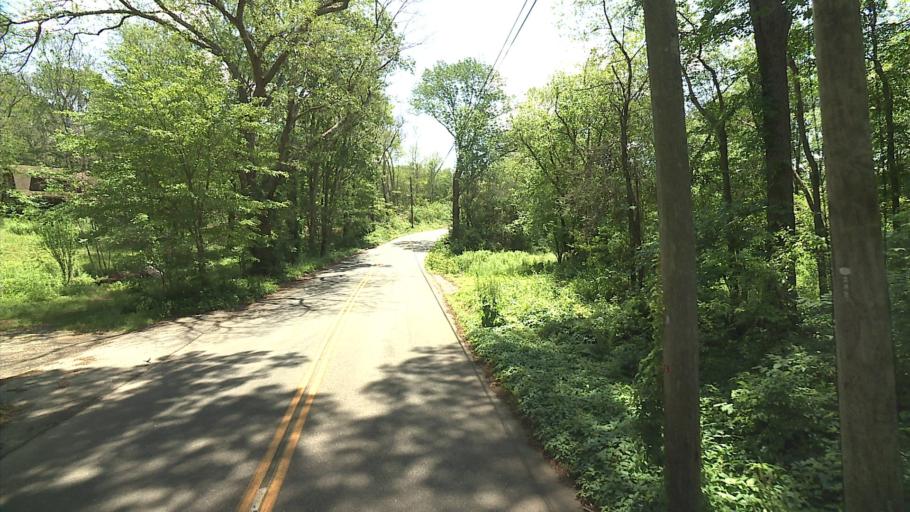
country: US
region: Connecticut
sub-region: New London County
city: Jewett City
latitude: 41.5998
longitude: -71.9050
